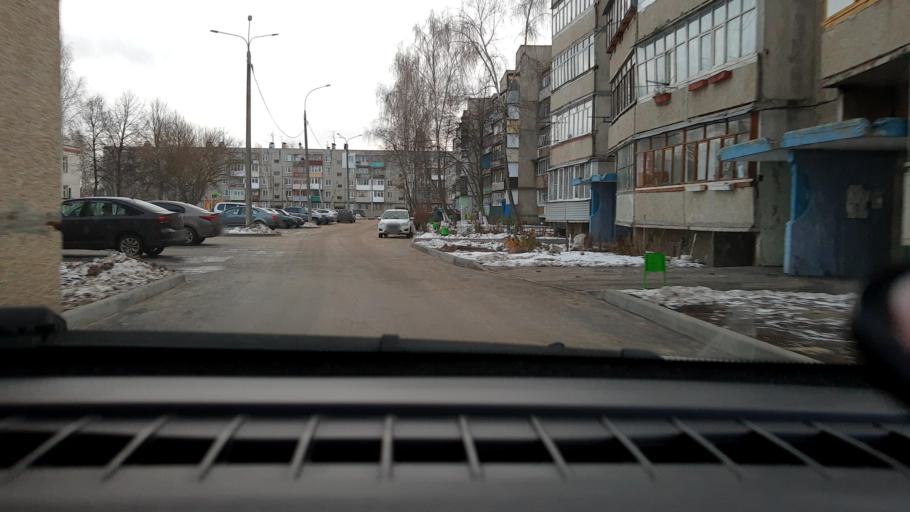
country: RU
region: Nizjnij Novgorod
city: Gorbatovka
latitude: 56.2453
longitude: 43.7458
